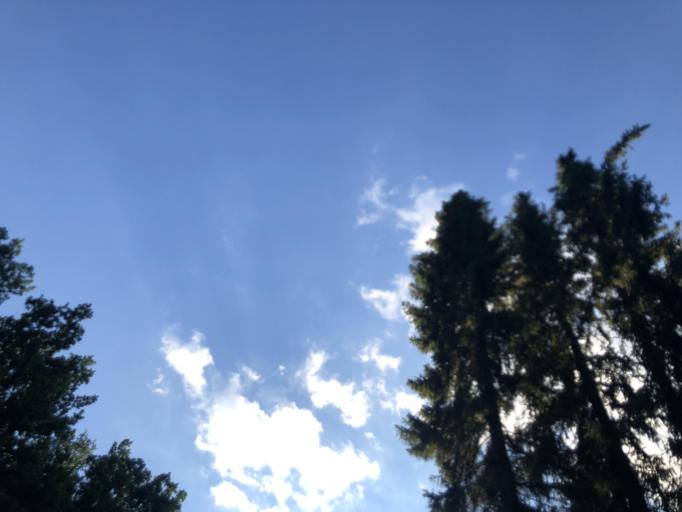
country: DE
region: Lower Saxony
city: Tosterglope
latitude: 53.2526
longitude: 10.7893
